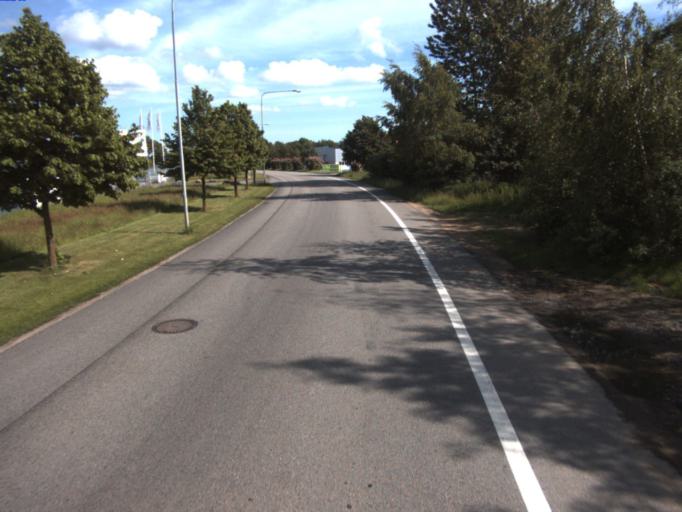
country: SE
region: Skane
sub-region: Helsingborg
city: Odakra
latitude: 56.0714
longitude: 12.7483
